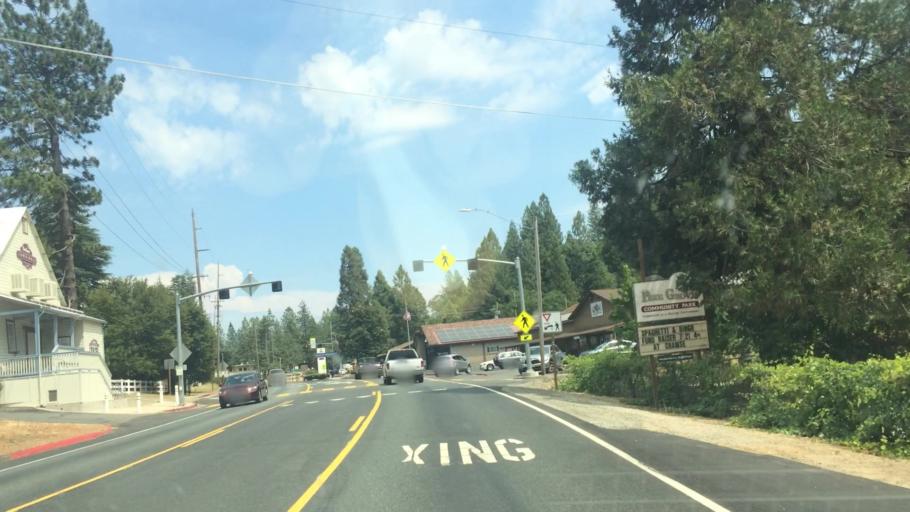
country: US
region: California
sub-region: Amador County
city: Pine Grove
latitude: 38.4132
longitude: -120.6584
